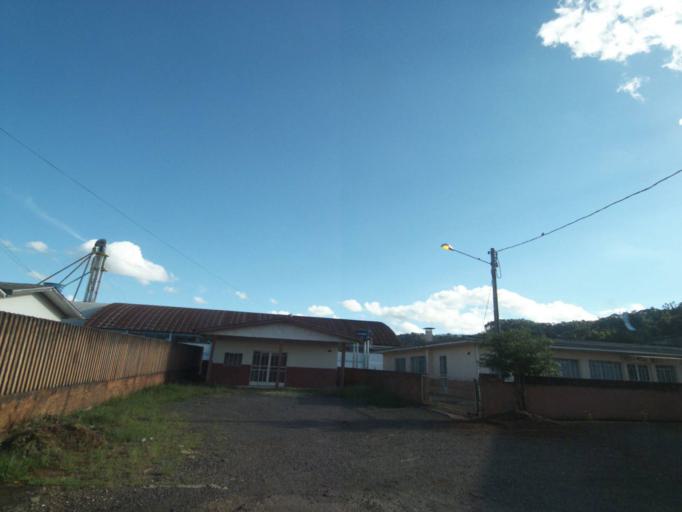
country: BR
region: Parana
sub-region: Uniao Da Vitoria
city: Uniao da Vitoria
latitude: -26.1614
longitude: -51.5368
